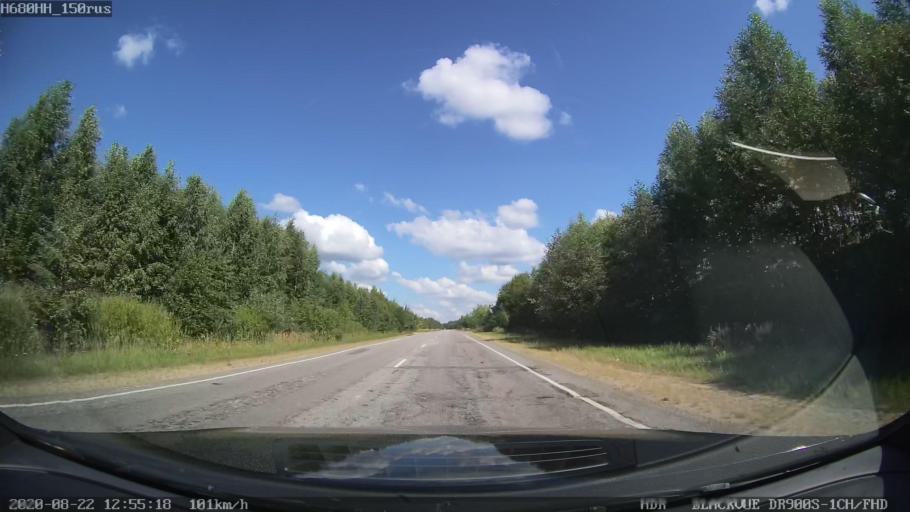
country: RU
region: Tverskaya
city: Rameshki
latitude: 57.5419
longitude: 36.2988
